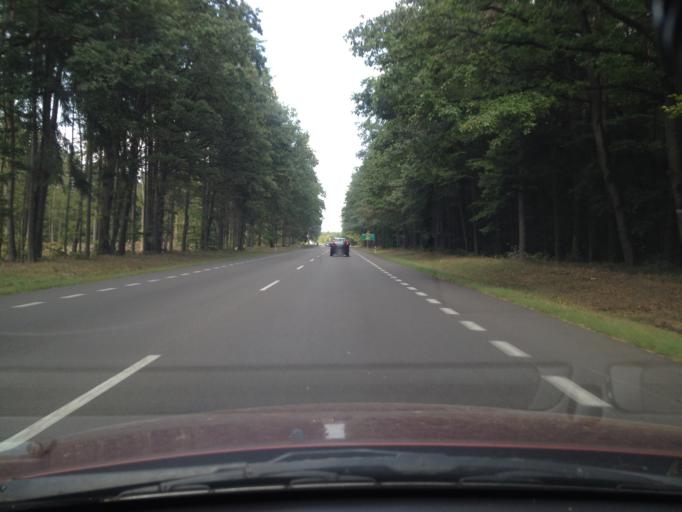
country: PL
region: West Pomeranian Voivodeship
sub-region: Powiat goleniowski
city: Przybiernow
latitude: 53.6718
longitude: 14.8140
